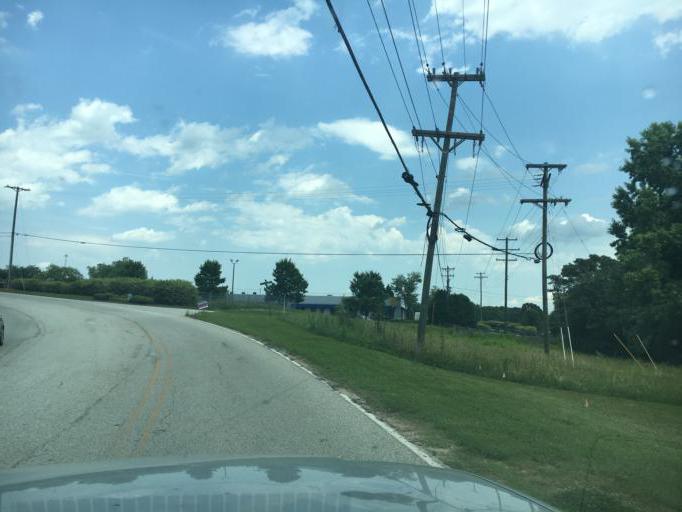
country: US
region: South Carolina
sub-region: Greenville County
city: Five Forks
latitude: 34.8714
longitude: -82.2313
